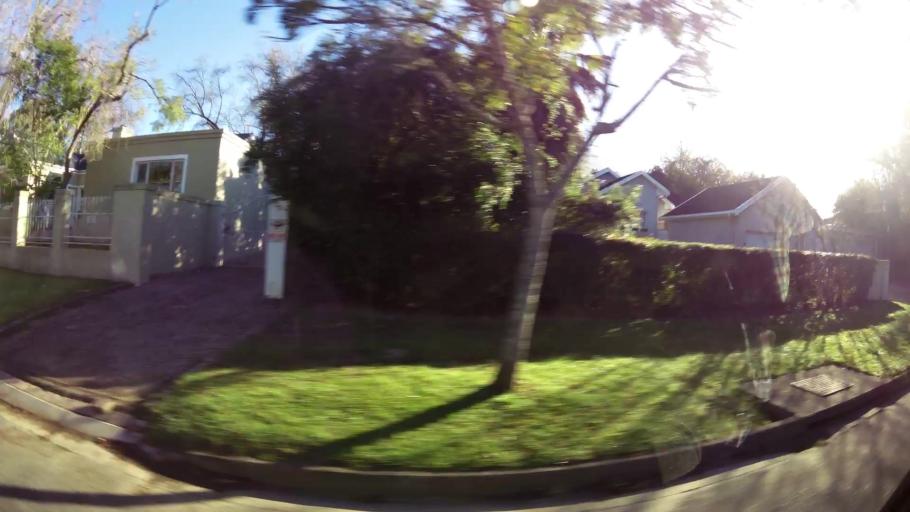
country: ZA
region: Western Cape
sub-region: Eden District Municipality
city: George
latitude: -33.9493
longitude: 22.4456
